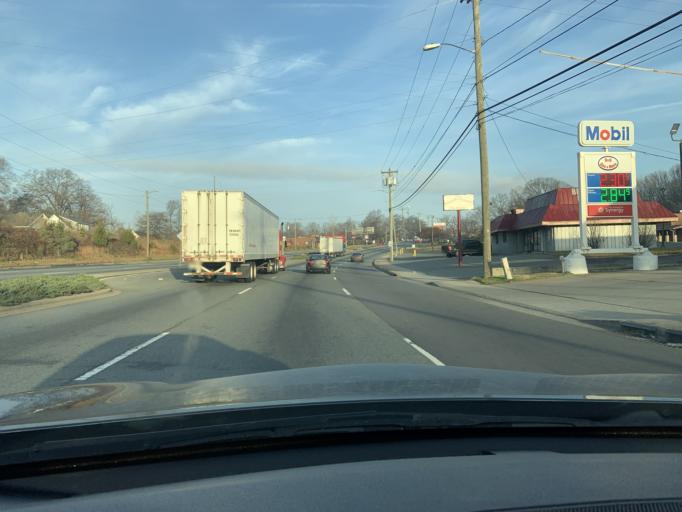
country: US
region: North Carolina
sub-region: Mecklenburg County
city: Charlotte
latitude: 35.2638
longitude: -80.8803
